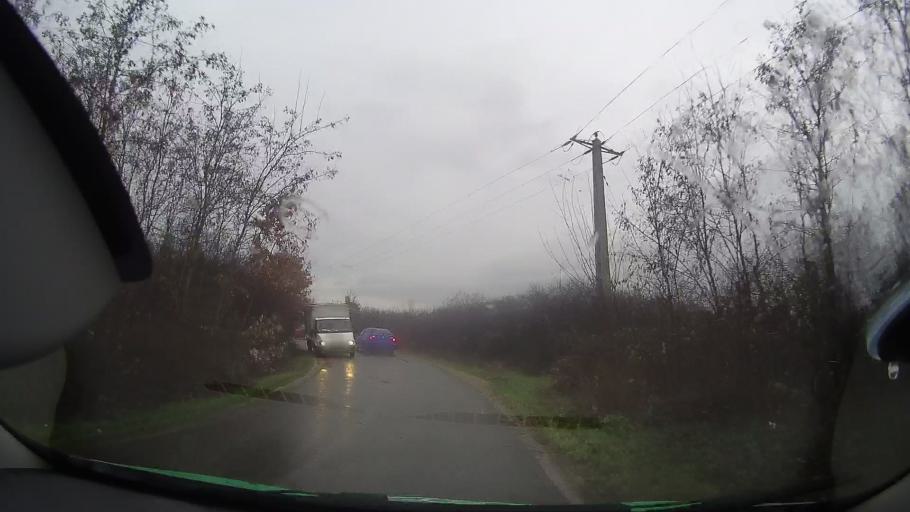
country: RO
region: Bihor
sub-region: Comuna Holod
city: Vintere
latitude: 46.7505
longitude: 22.1446
